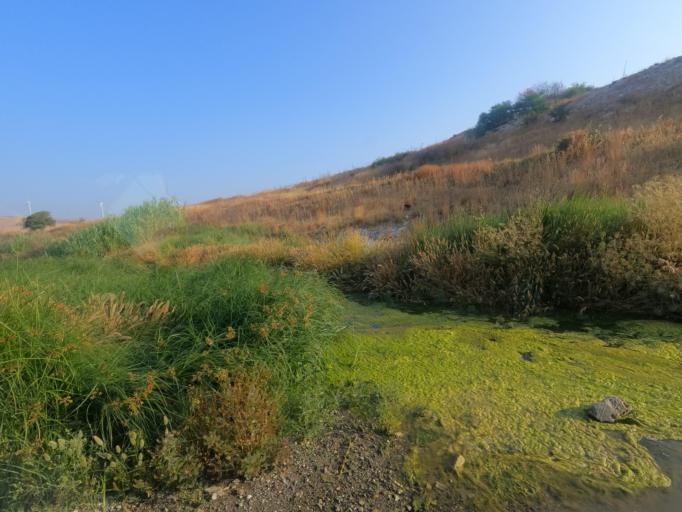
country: CY
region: Larnaka
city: Psevdas
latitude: 34.9179
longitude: 33.5123
